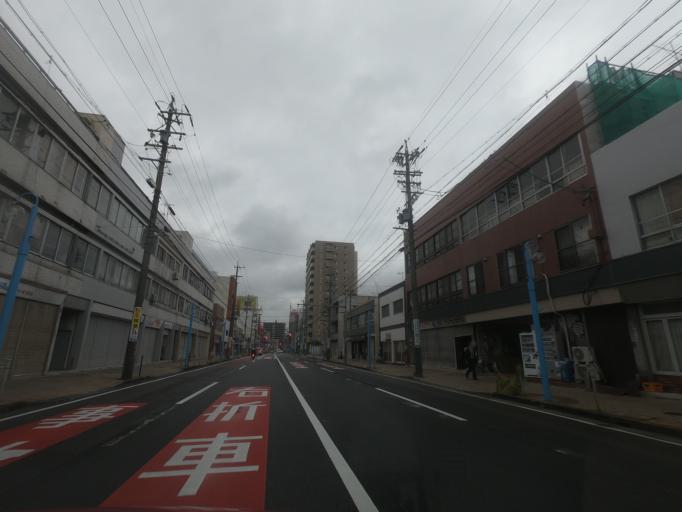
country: JP
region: Aichi
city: Kasugai
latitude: 35.2455
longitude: 136.9775
